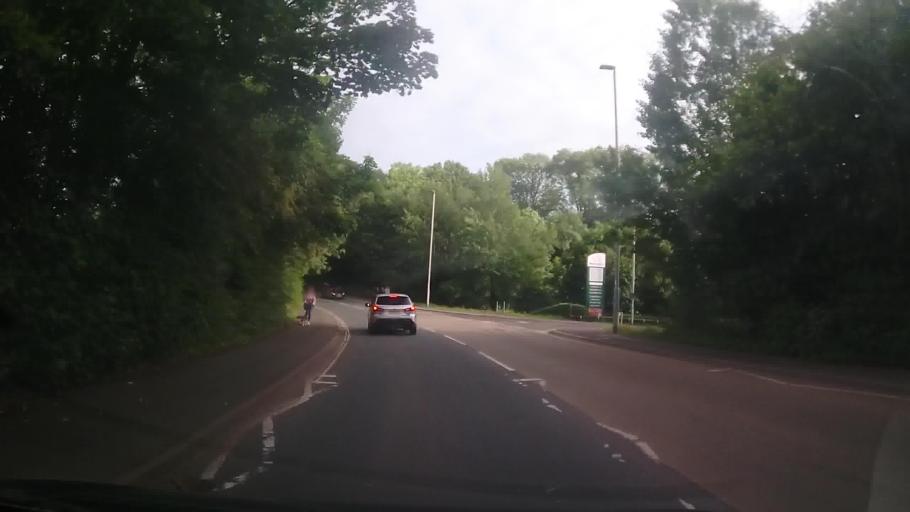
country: GB
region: England
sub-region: Devon
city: Kingsbridge
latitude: 50.2843
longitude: -3.7806
